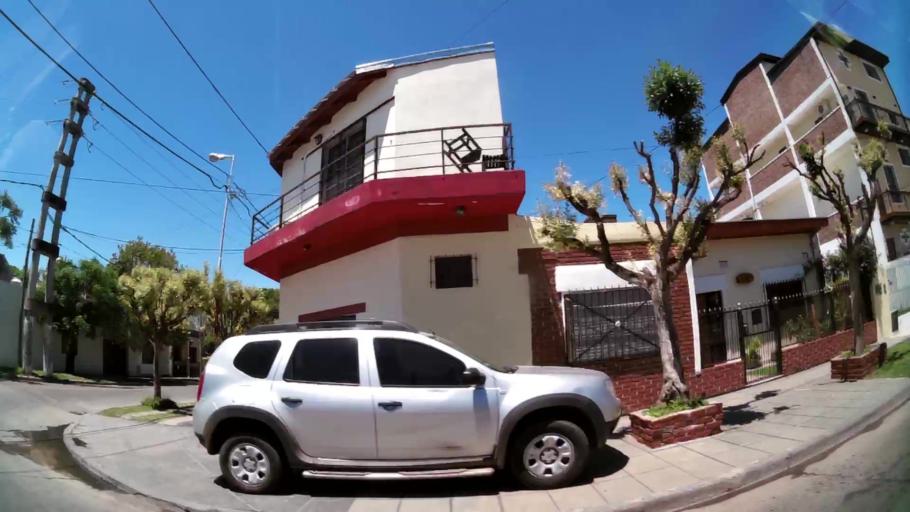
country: AR
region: Buenos Aires
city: Hurlingham
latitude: -34.4999
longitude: -58.6985
